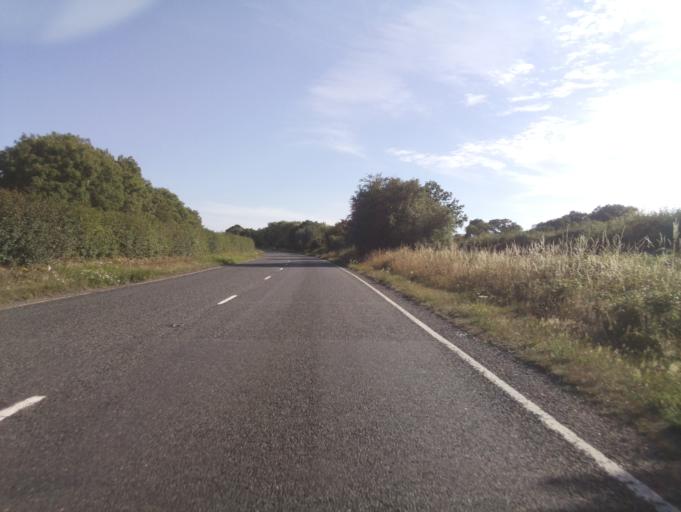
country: GB
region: England
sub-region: Hampshire
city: Romsey
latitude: 50.9731
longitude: -1.5210
